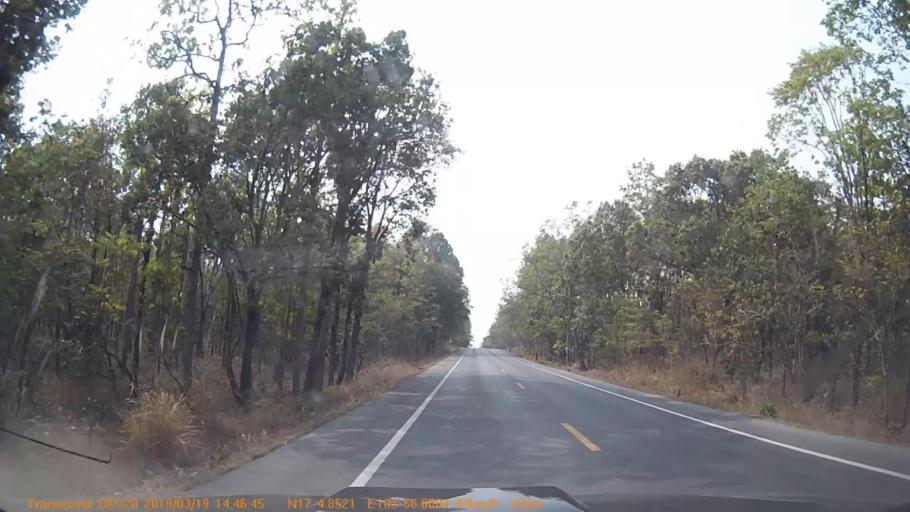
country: TH
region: Sakon Nakhon
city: Phu Phan
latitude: 17.0812
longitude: 103.9331
